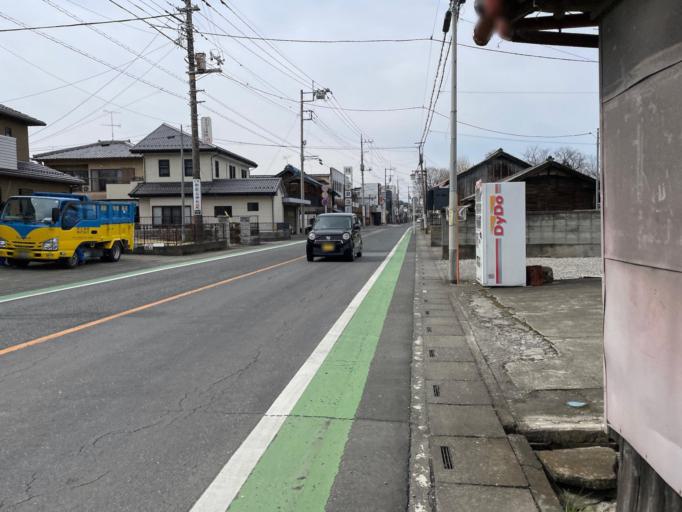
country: JP
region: Saitama
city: Kodamacho-kodamaminami
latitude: 36.1874
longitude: 139.1349
